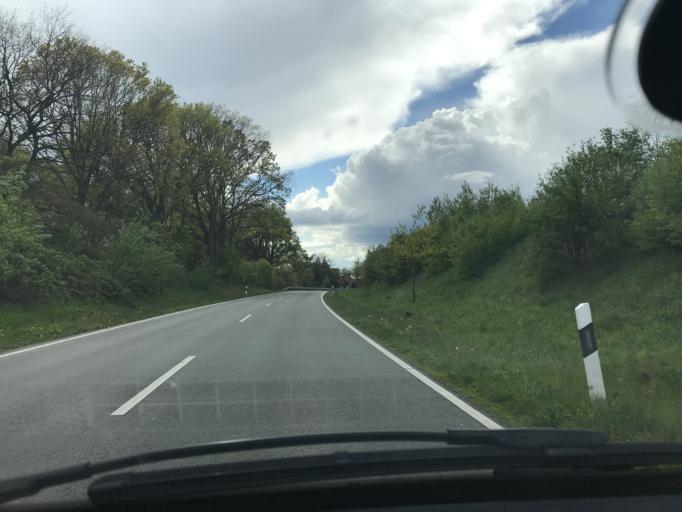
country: DE
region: Lower Saxony
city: Harsefeld
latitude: 53.4482
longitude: 9.5162
